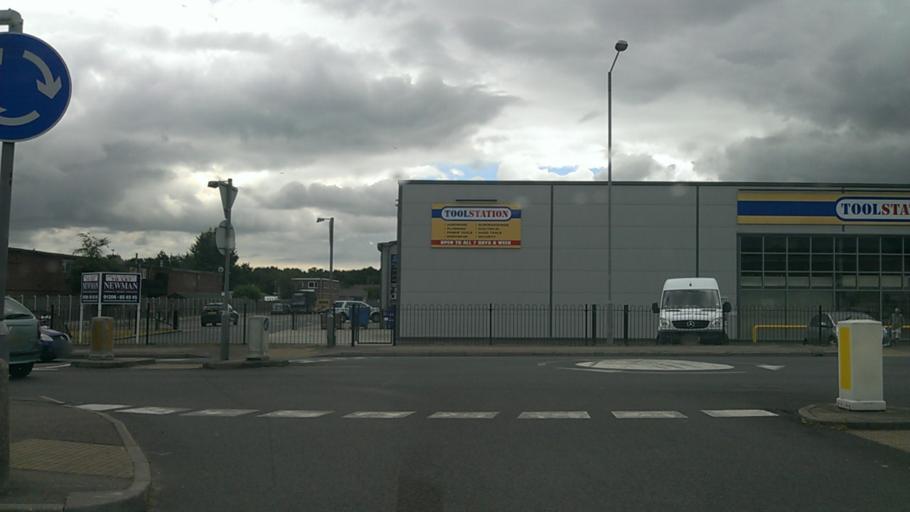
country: GB
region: England
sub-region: Essex
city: Eight Ash Green
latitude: 51.8779
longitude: 0.8456
